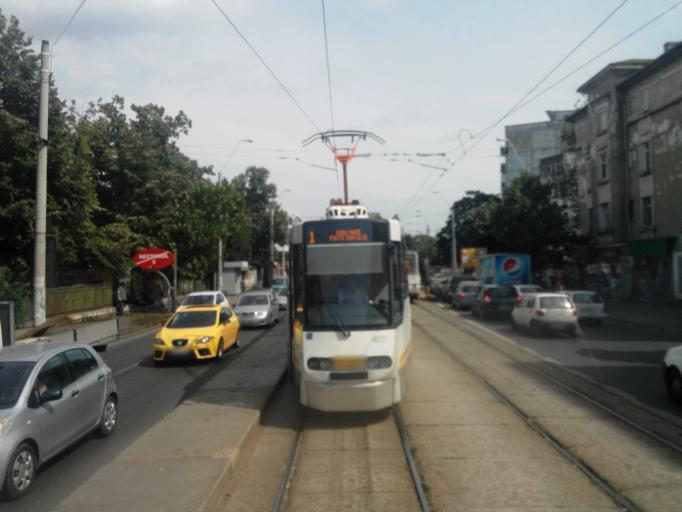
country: RO
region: Bucuresti
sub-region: Municipiul Bucuresti
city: Bucuresti
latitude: 44.4060
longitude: 26.0950
